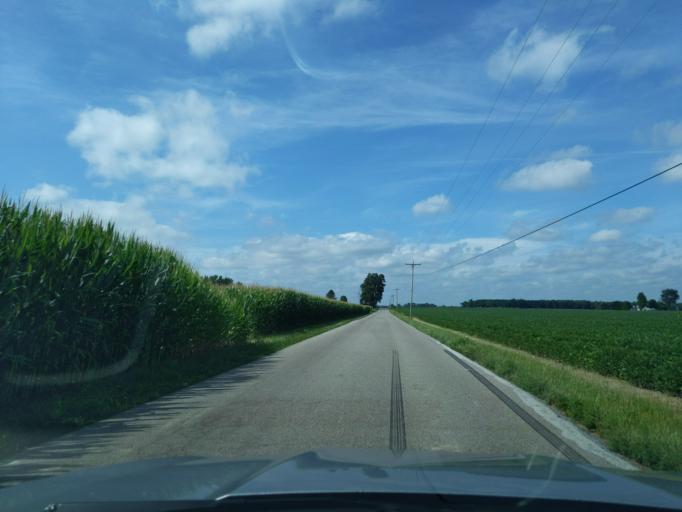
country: US
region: Indiana
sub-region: Ripley County
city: Batesville
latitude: 39.2826
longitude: -85.3477
